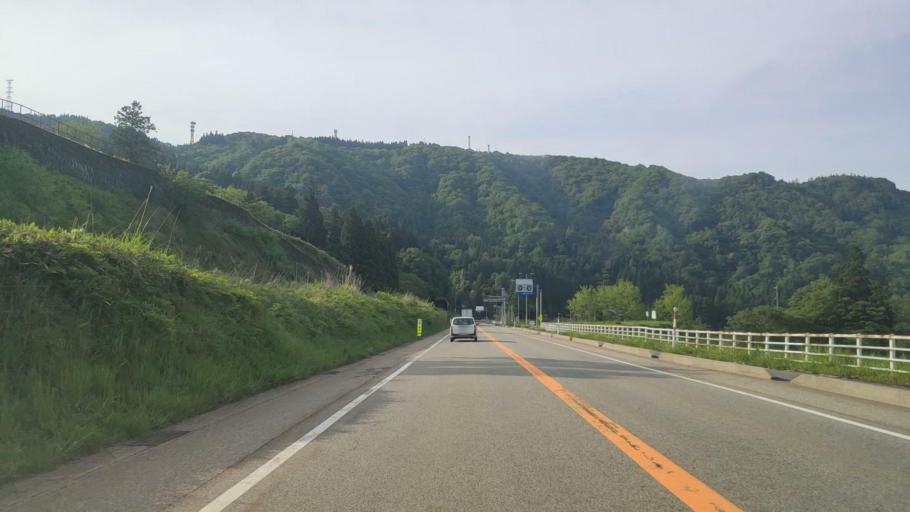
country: JP
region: Toyama
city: Yatsuomachi-higashikumisaka
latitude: 36.4914
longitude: 137.2368
